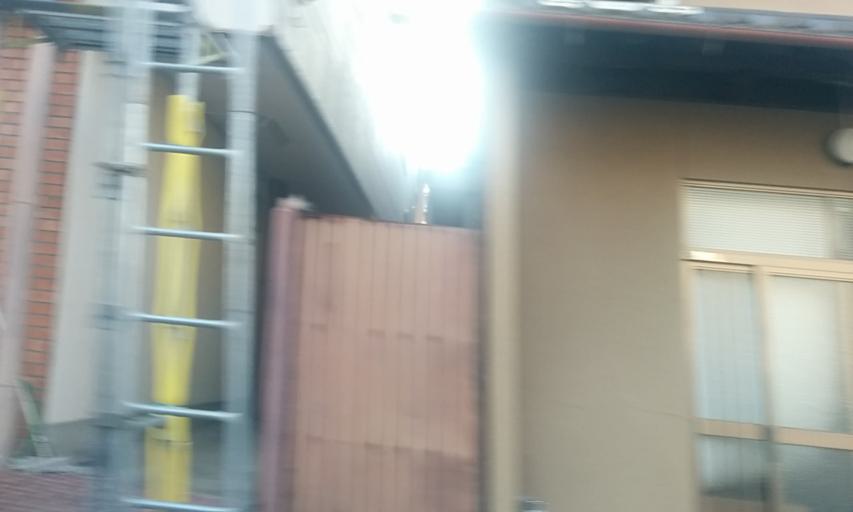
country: JP
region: Kyoto
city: Maizuru
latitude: 35.4446
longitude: 135.3261
